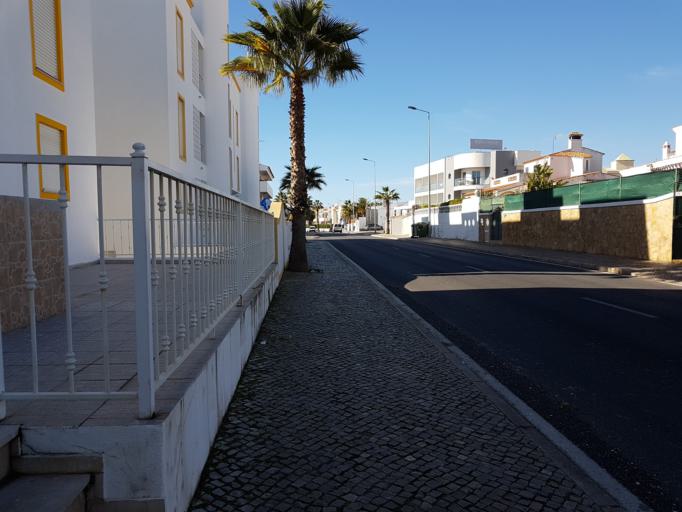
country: PT
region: Faro
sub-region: Albufeira
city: Albufeira
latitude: 37.0885
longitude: -8.2331
